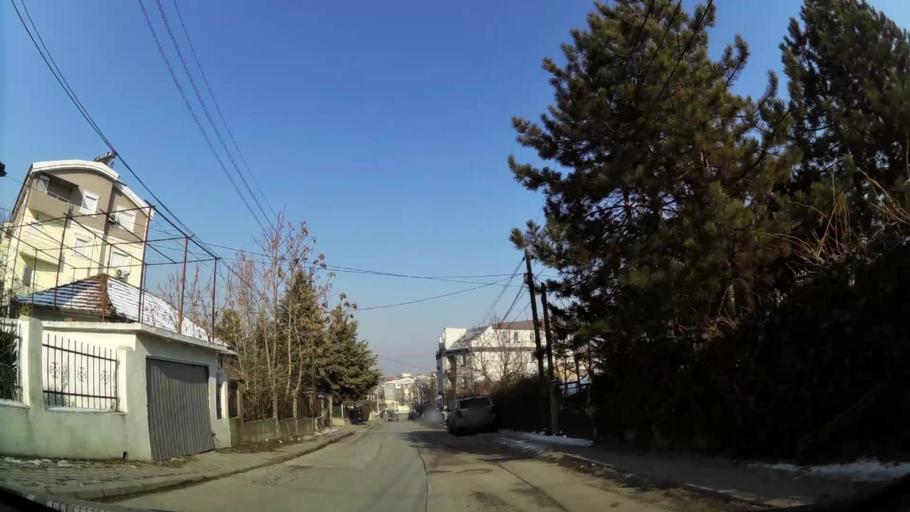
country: MK
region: Sopiste
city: Sopishte
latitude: 41.9742
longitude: 21.4382
